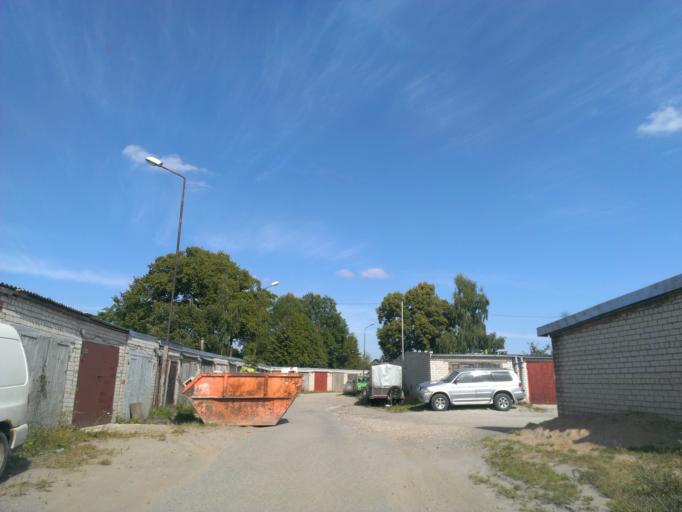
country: LV
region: Adazi
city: Adazi
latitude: 57.0829
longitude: 24.3195
